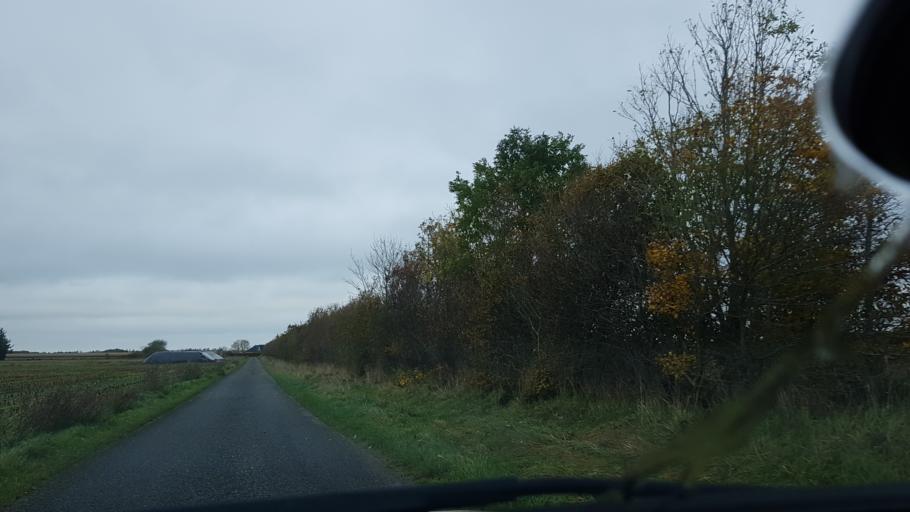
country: DK
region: South Denmark
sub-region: Esbjerg Kommune
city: Ribe
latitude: 55.2570
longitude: 8.8372
